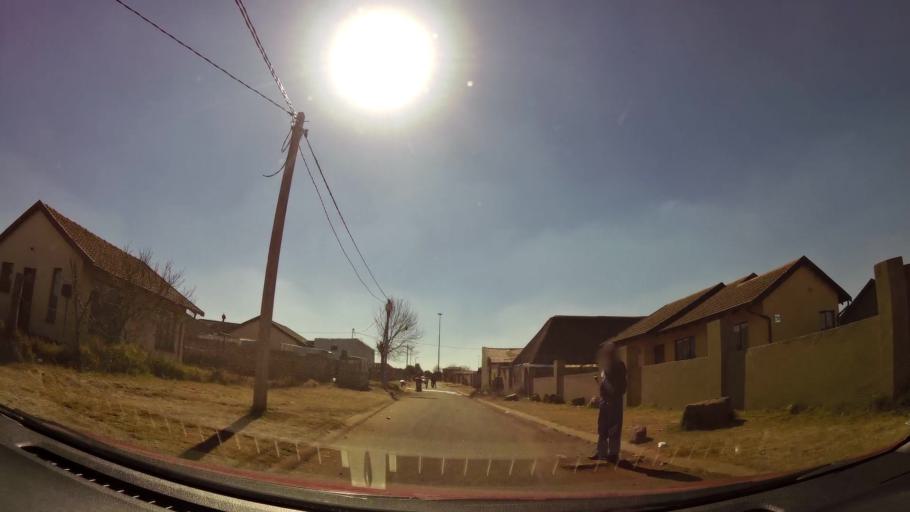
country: ZA
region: Gauteng
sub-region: City of Johannesburg Metropolitan Municipality
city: Soweto
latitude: -26.2459
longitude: 27.8058
